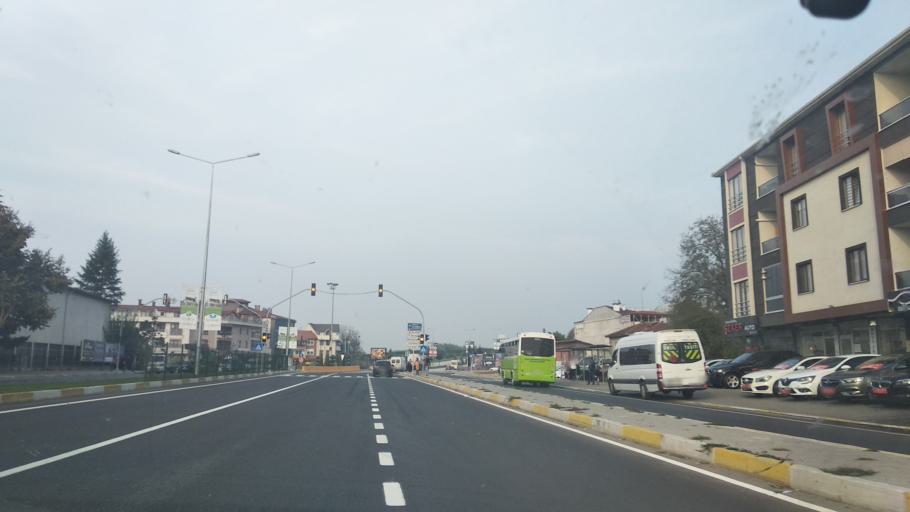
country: TR
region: Duzce
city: Duzce
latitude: 40.8349
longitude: 31.1705
